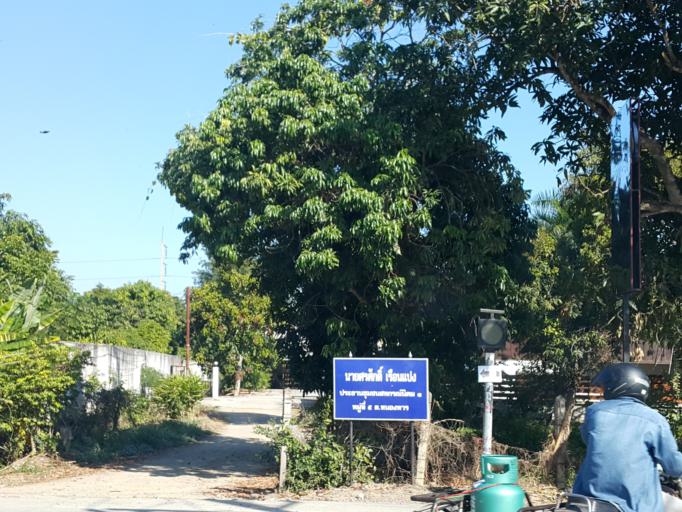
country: TH
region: Chiang Mai
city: San Sai
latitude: 18.8763
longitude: 99.0138
